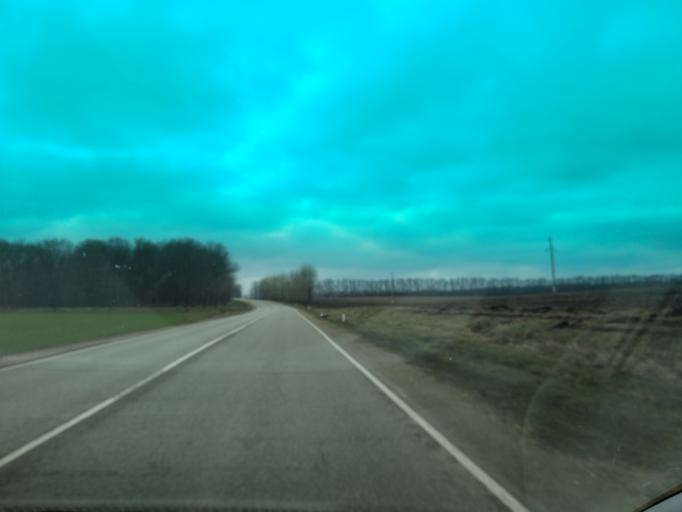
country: RU
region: Krasnodarskiy
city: Novorozhdestvenskaya
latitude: 45.7991
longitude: 39.9823
